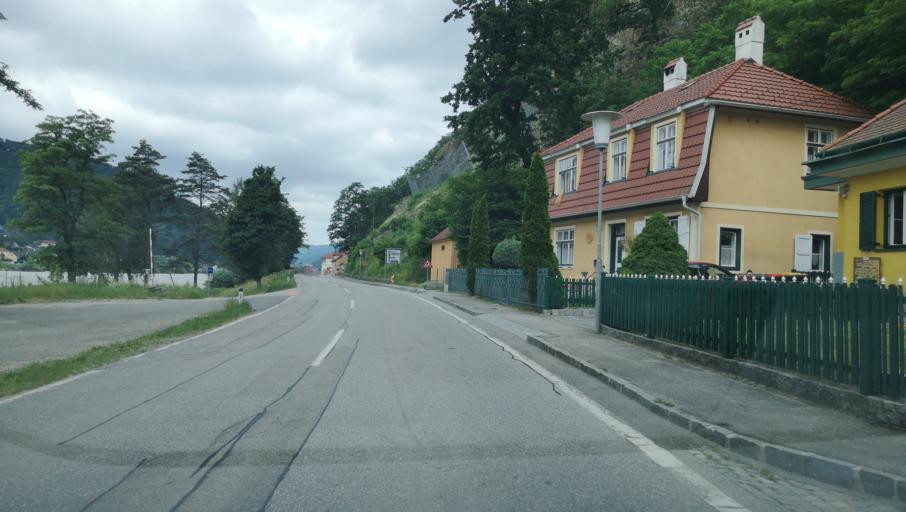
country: AT
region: Lower Austria
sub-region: Politischer Bezirk Krems
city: Aggsbach
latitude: 48.2878
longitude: 15.4065
